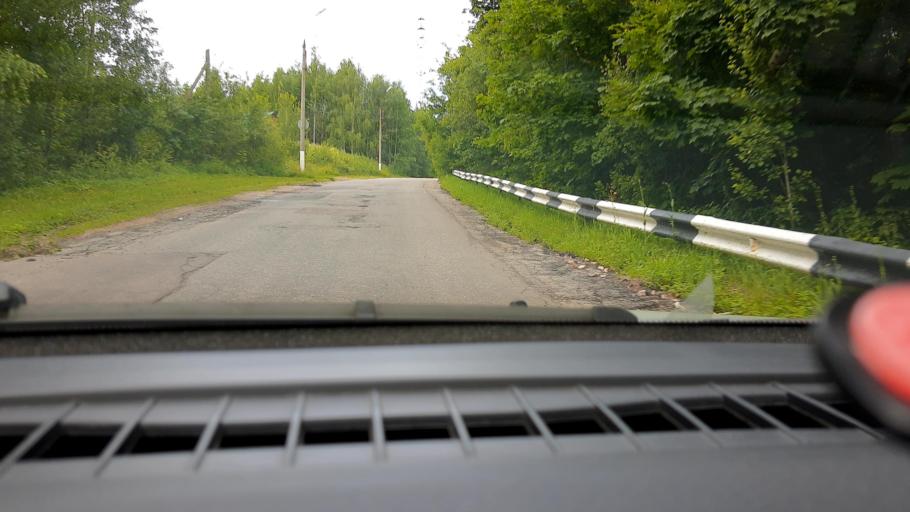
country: RU
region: Nizjnij Novgorod
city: Kstovo
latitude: 56.1470
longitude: 44.3366
